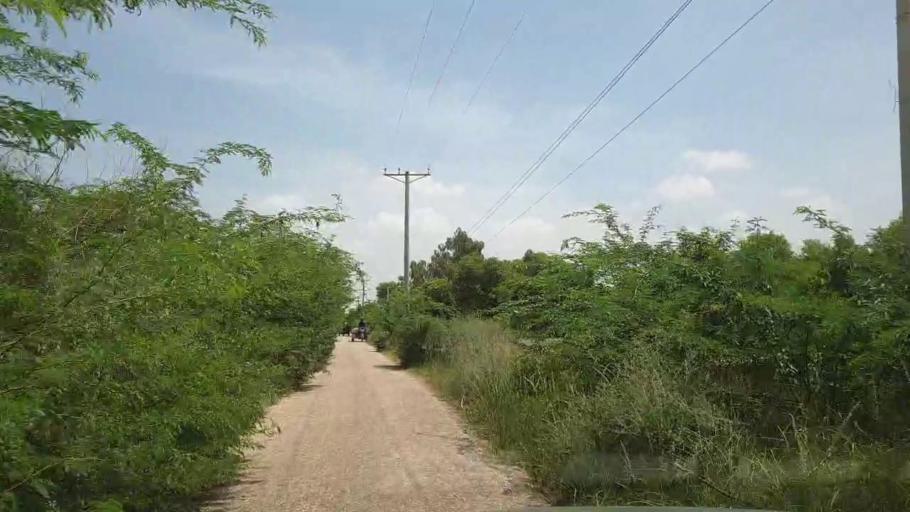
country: PK
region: Sindh
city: Kot Diji
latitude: 27.1302
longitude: 69.0024
